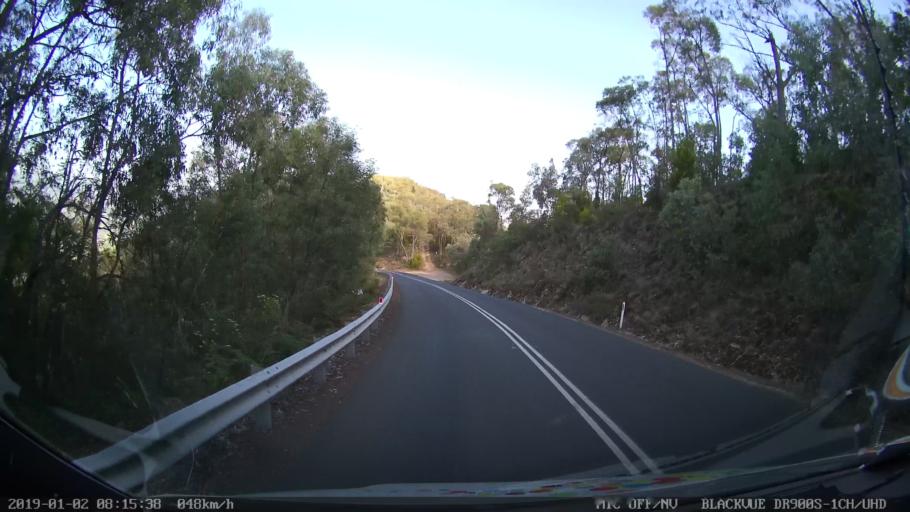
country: AU
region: New South Wales
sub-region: Tumut Shire
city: Tumut
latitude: -35.5815
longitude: 148.3367
